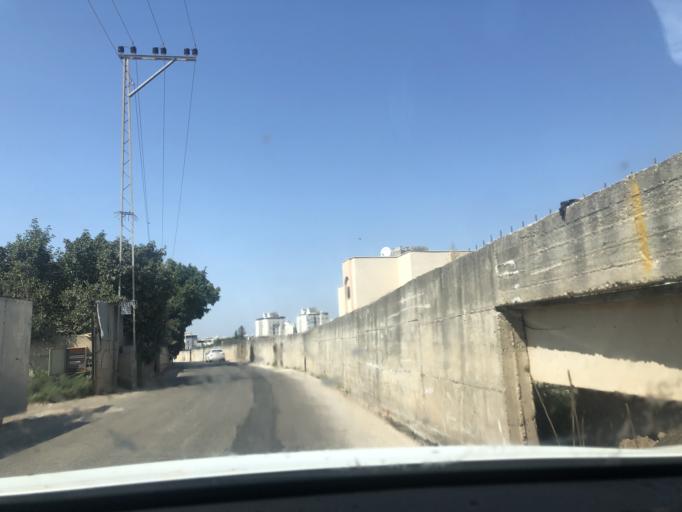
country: IL
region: Central District
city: Lod
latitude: 31.9542
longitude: 34.8807
